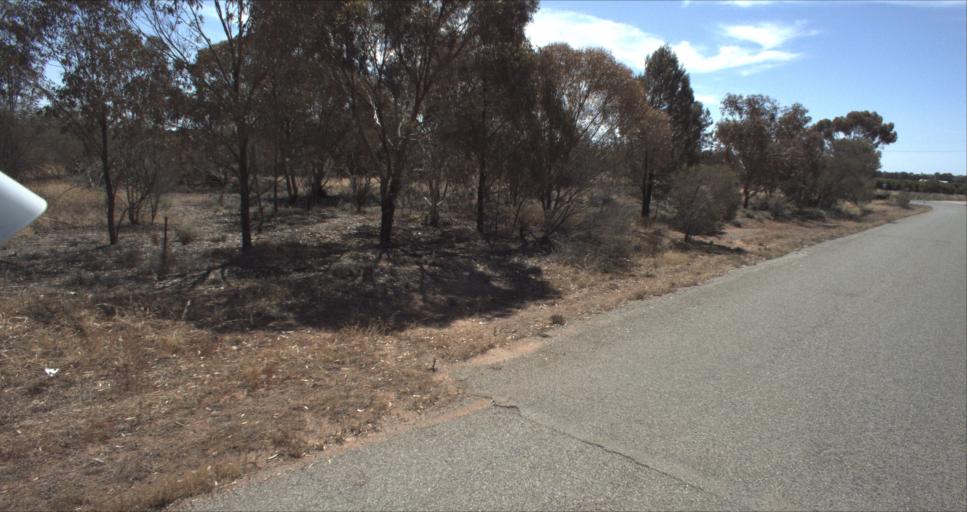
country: AU
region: New South Wales
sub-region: Leeton
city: Leeton
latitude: -34.6078
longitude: 146.4351
